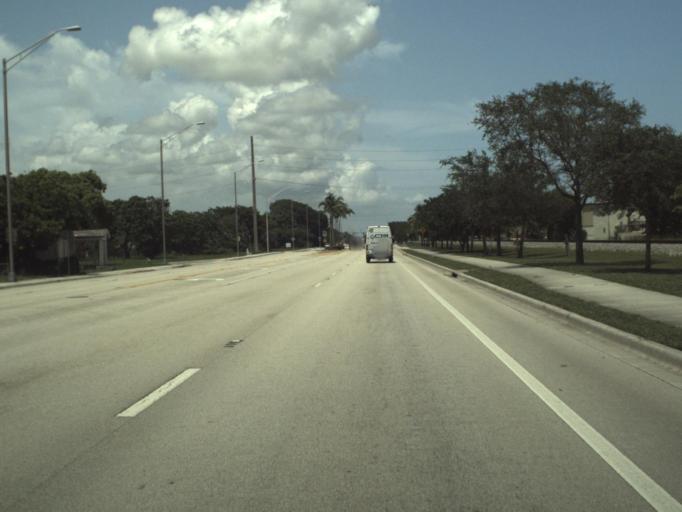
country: US
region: Florida
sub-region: Broward County
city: Deerfield Beach
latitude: 26.3071
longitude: -80.1046
